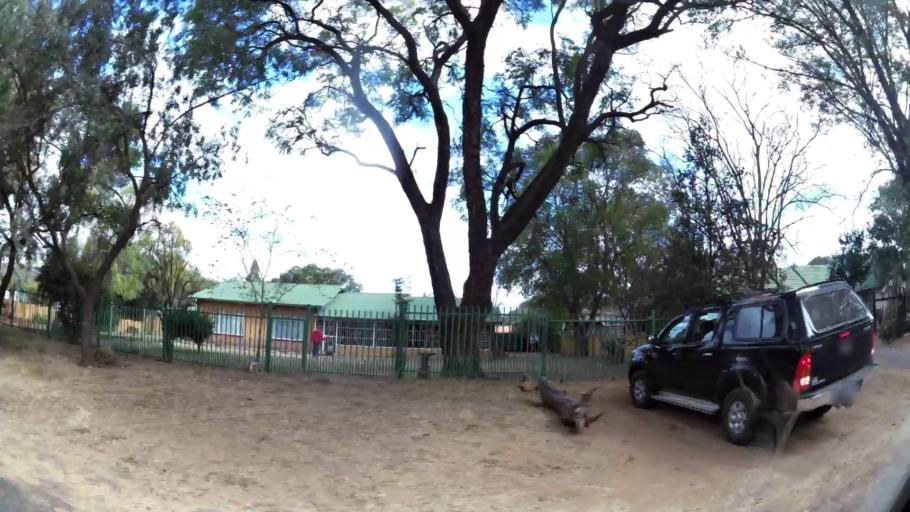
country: ZA
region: Limpopo
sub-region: Waterberg District Municipality
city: Modimolle
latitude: -24.7092
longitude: 28.4071
